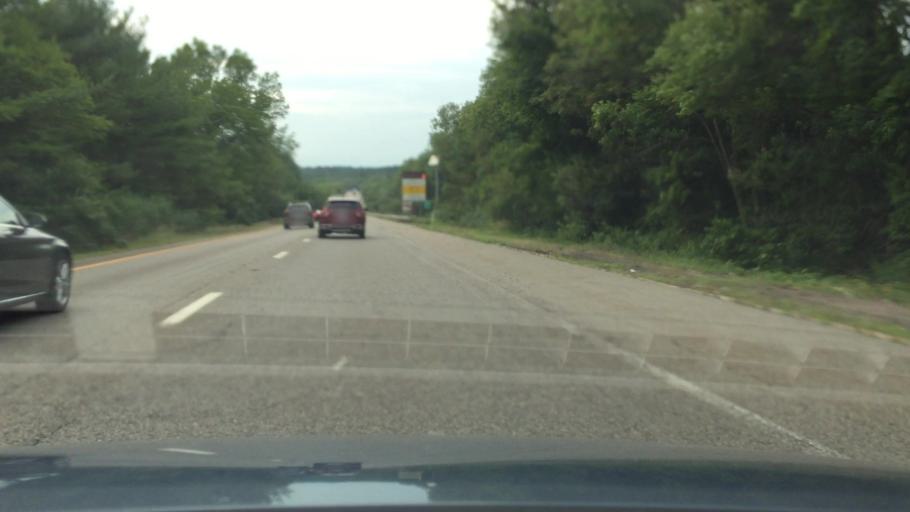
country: US
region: Massachusetts
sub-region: Plymouth County
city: North Pembroke
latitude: 42.1116
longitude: -70.7713
